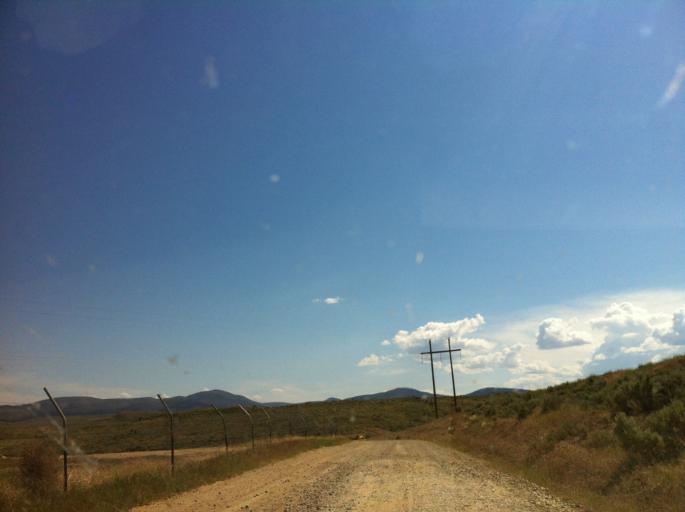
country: US
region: Oregon
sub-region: Baker County
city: Baker City
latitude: 44.7064
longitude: -117.7881
